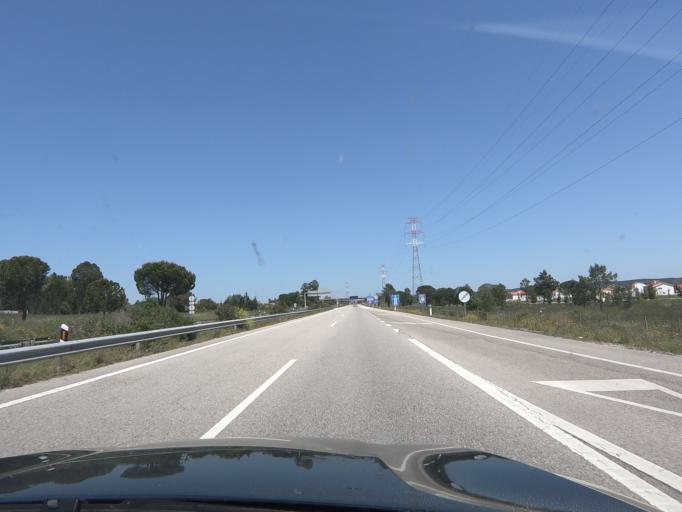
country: PT
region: Santarem
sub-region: Entroncamento
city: Entroncamento
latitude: 39.4759
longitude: -8.4864
